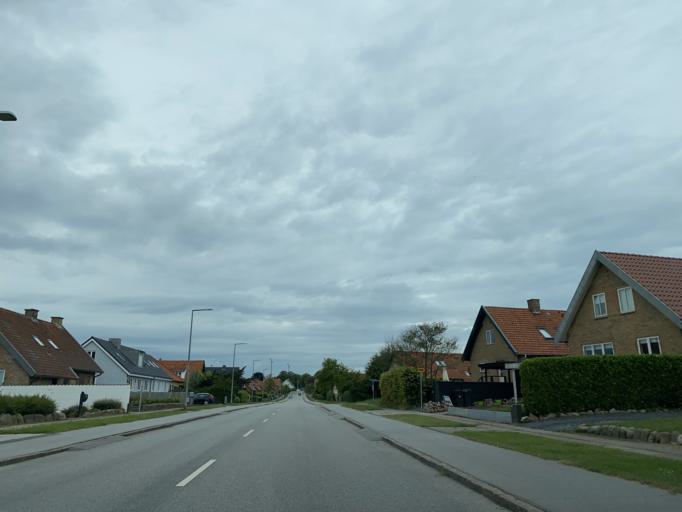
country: DK
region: South Denmark
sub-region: Sonderborg Kommune
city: Sonderborg
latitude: 54.9042
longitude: 9.8076
